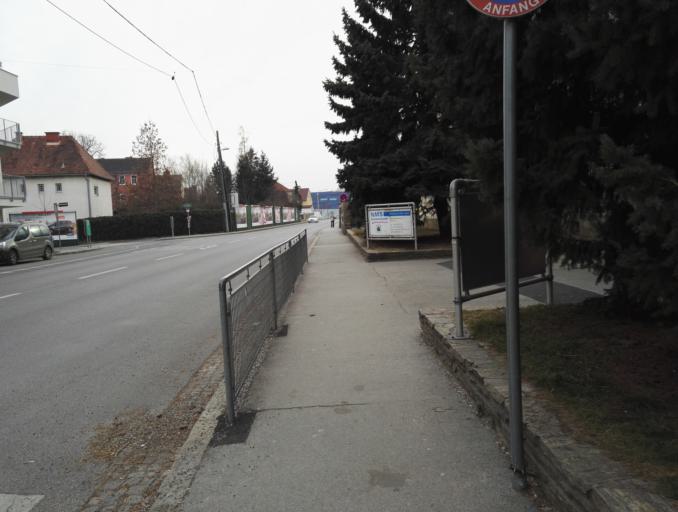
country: AT
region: Styria
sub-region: Graz Stadt
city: Wetzelsdorf
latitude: 47.0748
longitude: 15.4013
